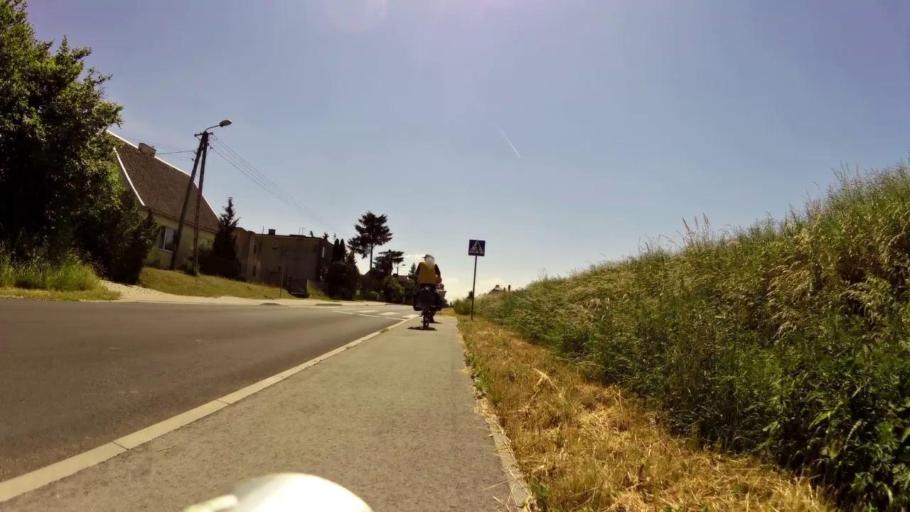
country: PL
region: Kujawsko-Pomorskie
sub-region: Powiat nakielski
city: Slesin
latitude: 53.1688
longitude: 17.7052
